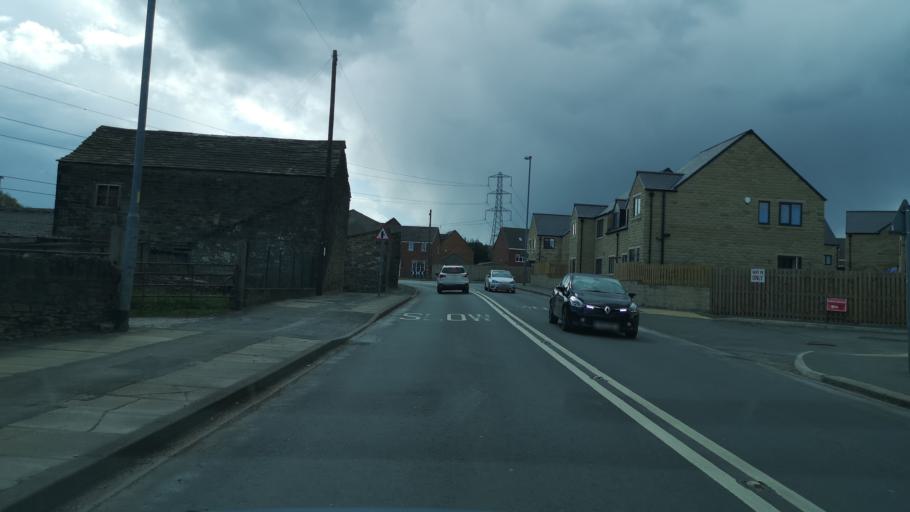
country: GB
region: England
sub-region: City and Borough of Wakefield
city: Horbury
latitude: 53.6676
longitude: -1.5701
